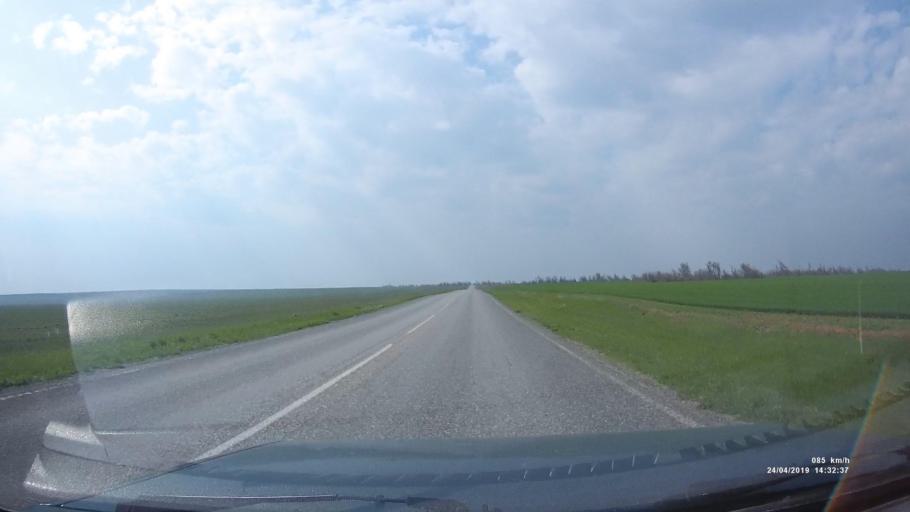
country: RU
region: Kalmykiya
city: Arshan'
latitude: 46.3661
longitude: 43.9663
